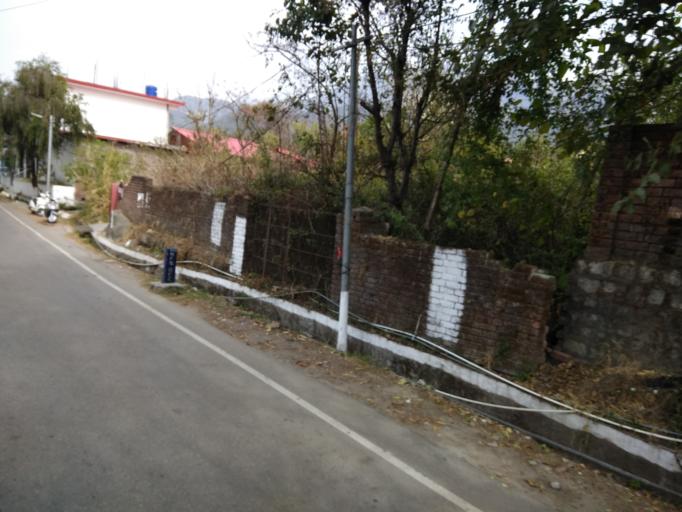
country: IN
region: Himachal Pradesh
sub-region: Kangra
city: Dharmsala
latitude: 32.1961
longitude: 76.3442
